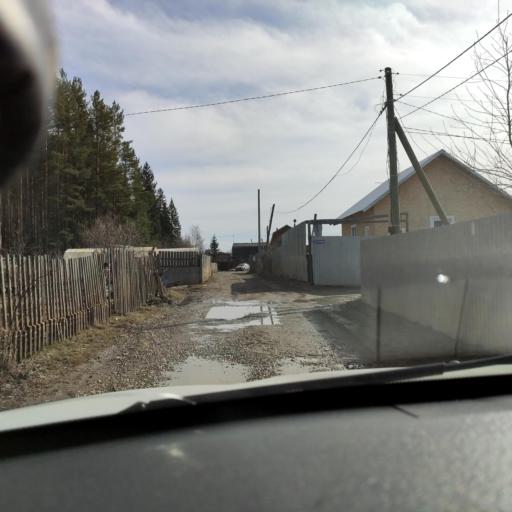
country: RU
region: Perm
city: Overyata
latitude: 58.0594
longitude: 55.9866
